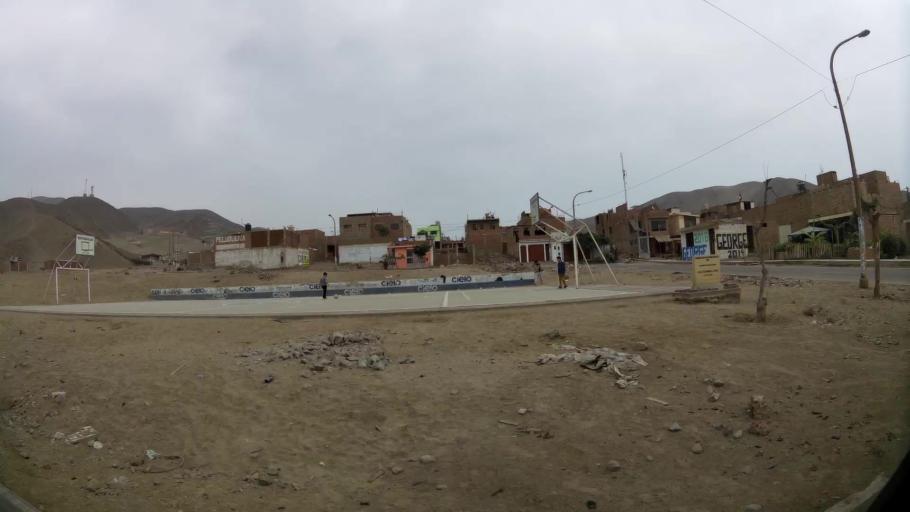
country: PE
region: Lima
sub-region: Lima
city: Santa Rosa
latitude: -11.7896
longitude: -77.1554
